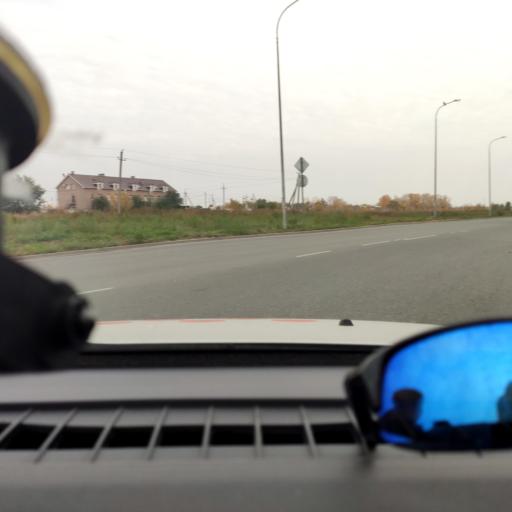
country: RU
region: Samara
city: Samara
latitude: 53.0964
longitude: 50.1612
